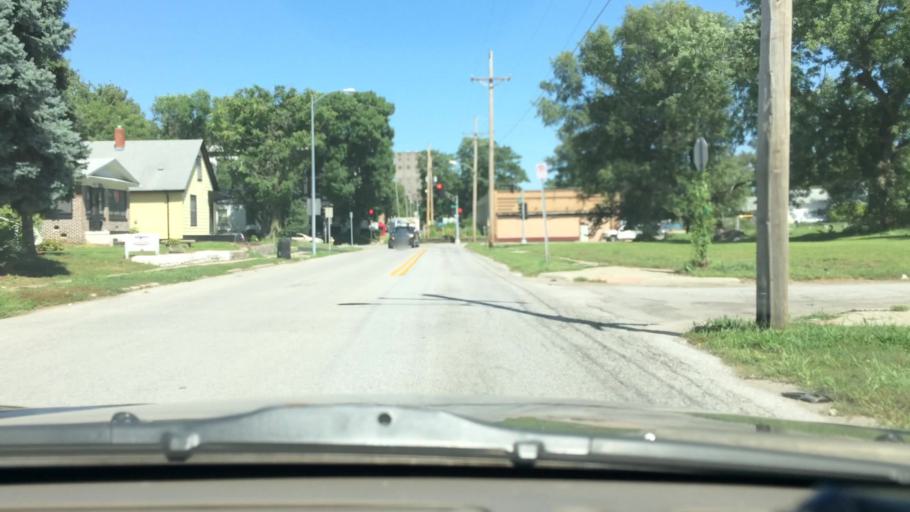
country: US
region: Iowa
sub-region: Pottawattamie County
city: Carter Lake
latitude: 41.2815
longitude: -95.9384
